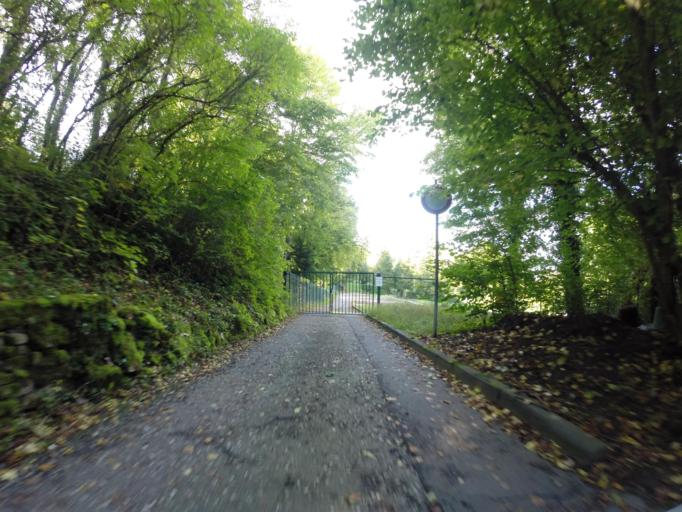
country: DE
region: Thuringia
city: Jena
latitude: 50.9426
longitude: 11.5886
